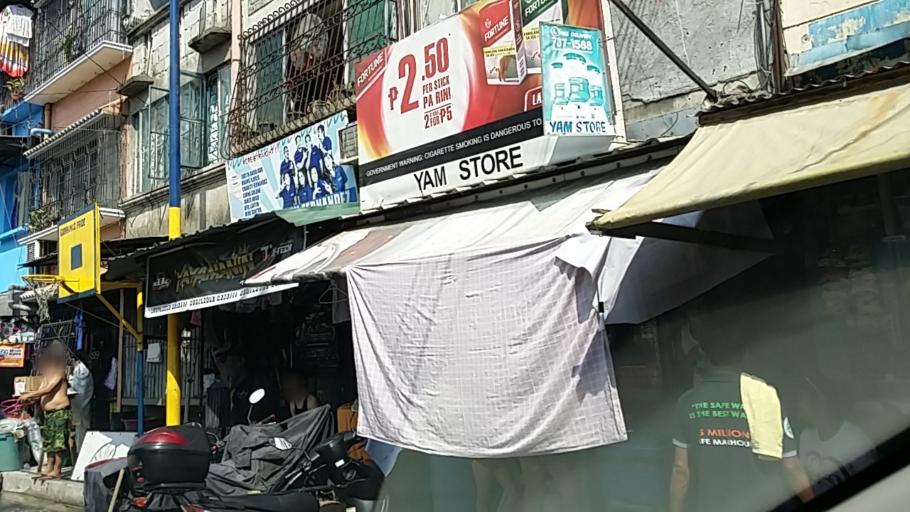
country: PH
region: Metro Manila
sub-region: Mandaluyong
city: Mandaluyong City
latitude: 14.5751
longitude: 121.0394
